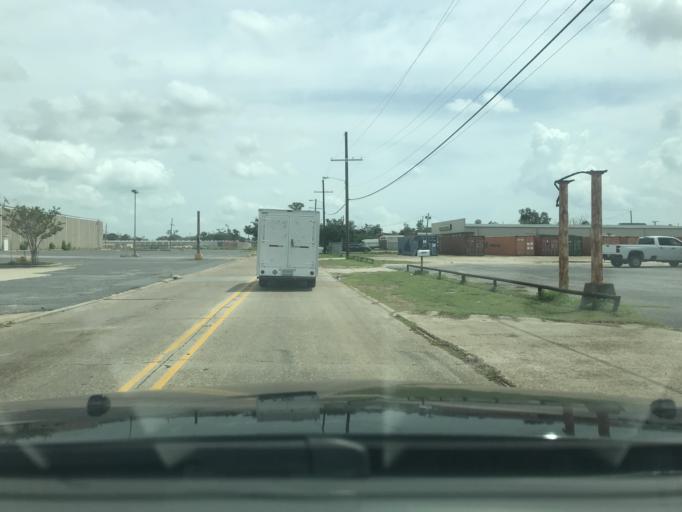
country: US
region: Louisiana
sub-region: Calcasieu Parish
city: Lake Charles
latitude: 30.2130
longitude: -93.2141
